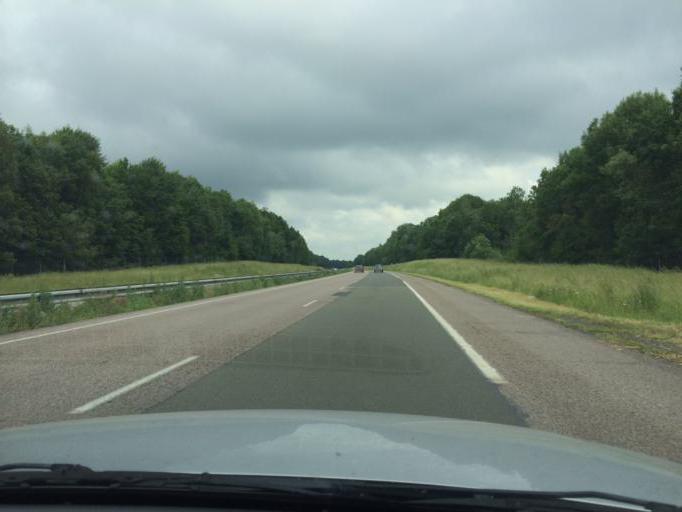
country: FR
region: Picardie
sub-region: Departement de l'Aisne
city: Crezancy
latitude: 49.1141
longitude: 3.5029
